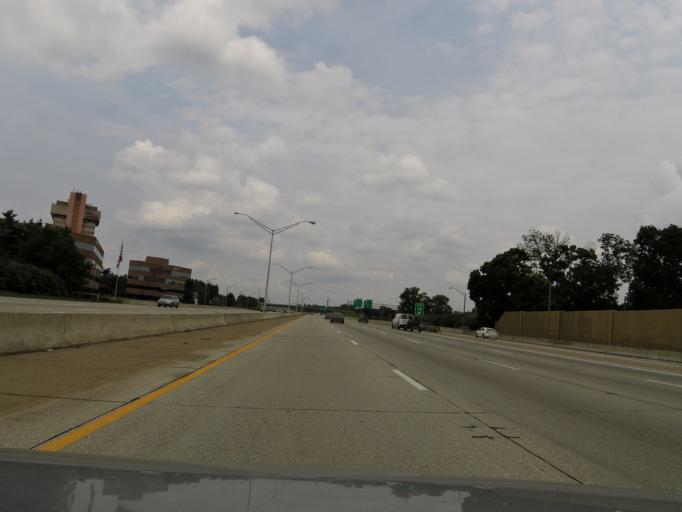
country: US
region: Kentucky
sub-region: Jefferson County
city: Saint Regis Park
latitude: 38.2256
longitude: -85.6417
